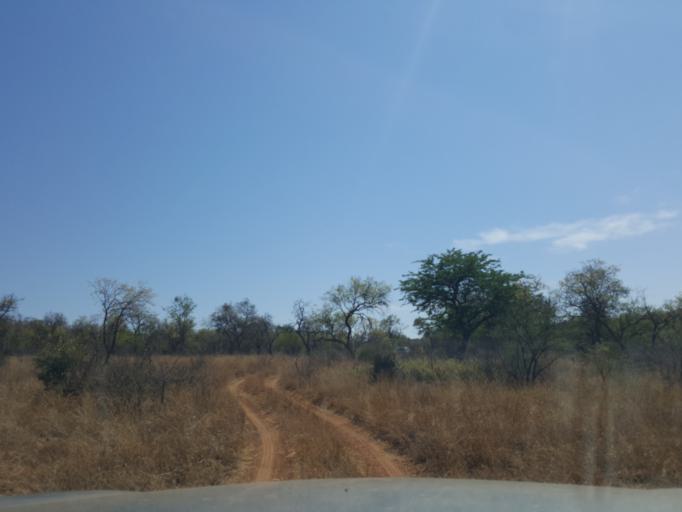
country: BW
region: South East
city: Lobatse
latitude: -25.1429
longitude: 25.6698
